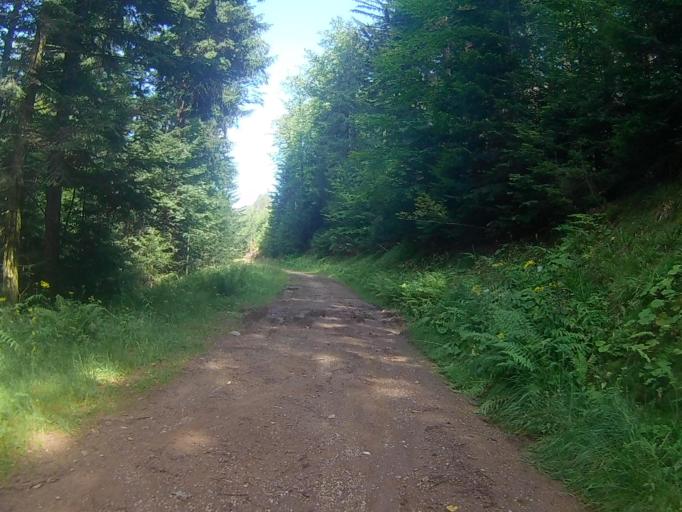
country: SI
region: Ruse
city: Ruse
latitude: 46.5074
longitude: 15.5447
